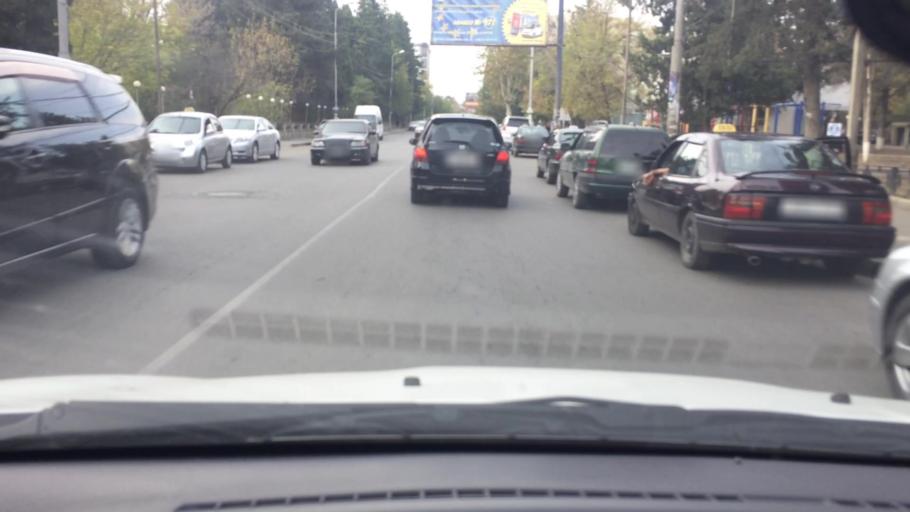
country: GE
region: Kvemo Kartli
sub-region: Marneuli
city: Marneuli
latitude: 41.4737
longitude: 44.8138
